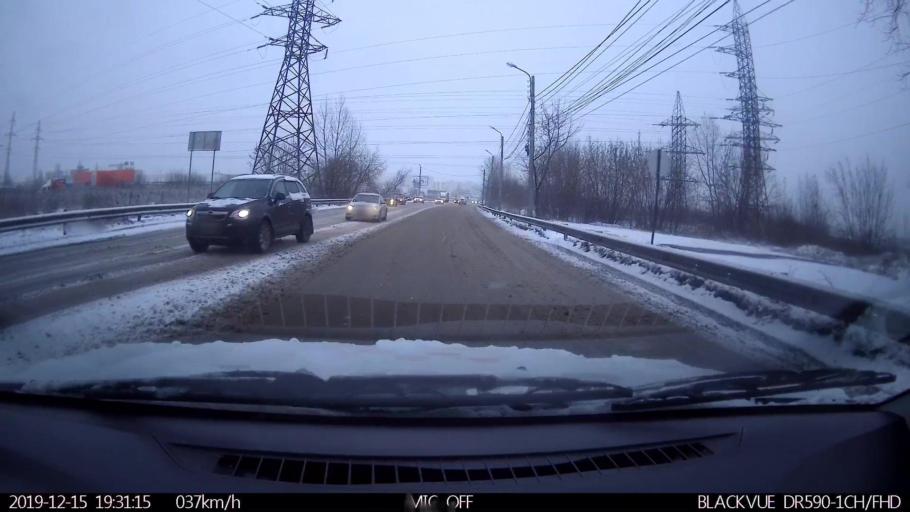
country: RU
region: Nizjnij Novgorod
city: Neklyudovo
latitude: 56.3446
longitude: 43.8899
